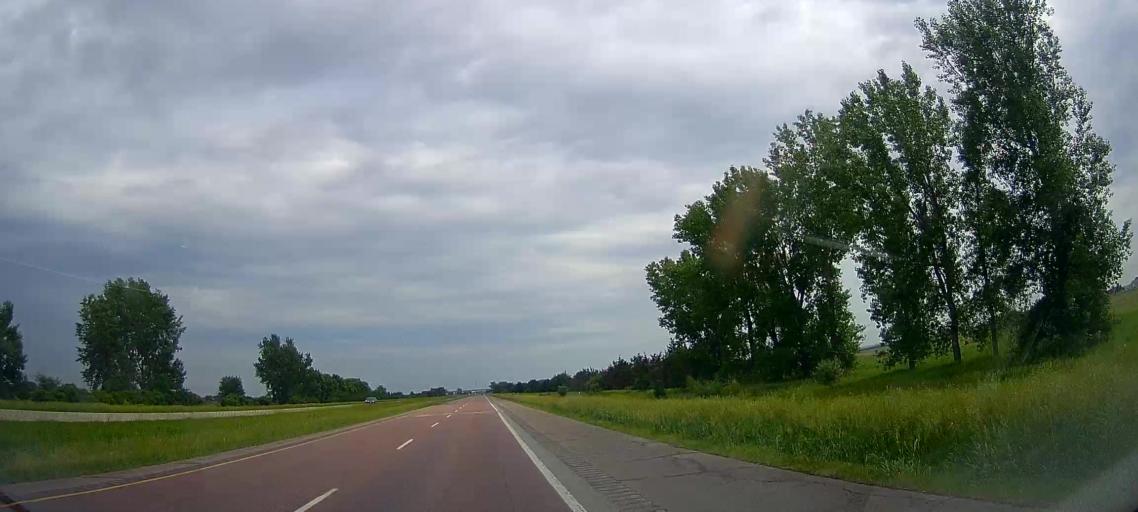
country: US
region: Iowa
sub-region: Woodbury County
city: Sergeant Bluff
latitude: 42.2644
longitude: -96.2636
